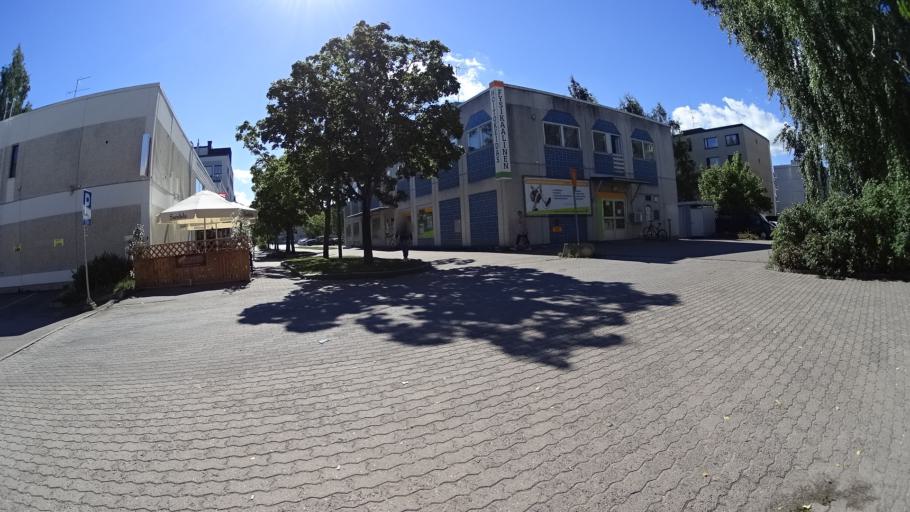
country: FI
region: Uusimaa
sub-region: Helsinki
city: Jaervenpaeae
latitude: 60.4728
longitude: 25.0856
